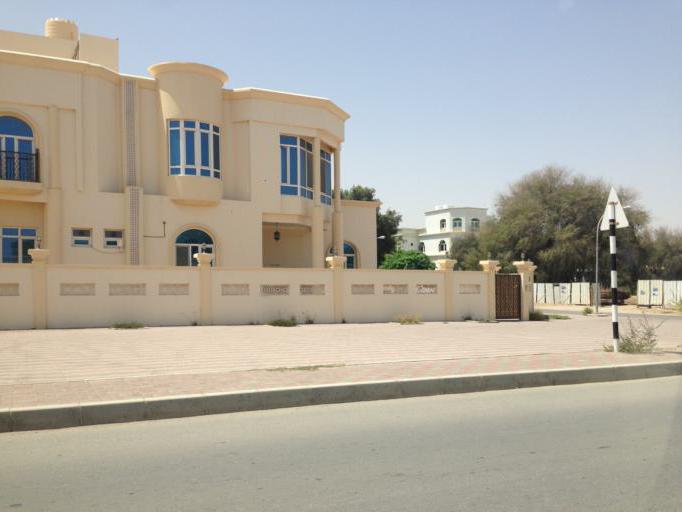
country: OM
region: Muhafazat Masqat
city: Bawshar
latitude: 23.6040
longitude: 58.3585
